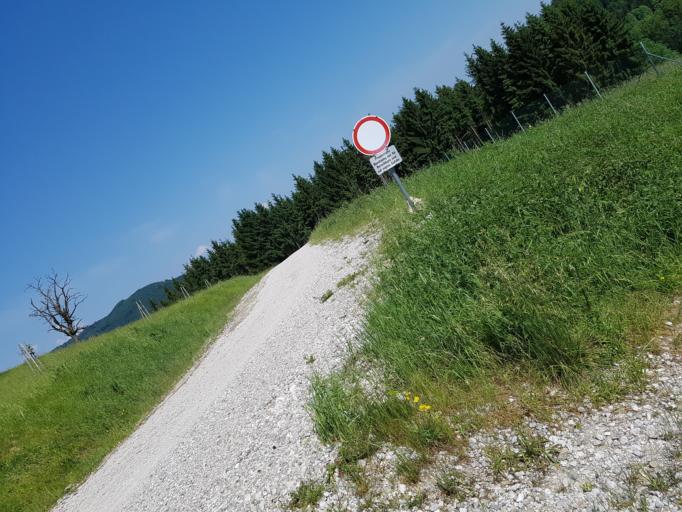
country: AT
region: Upper Austria
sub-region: Politischer Bezirk Gmunden
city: Altmunster
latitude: 47.9183
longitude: 13.7619
